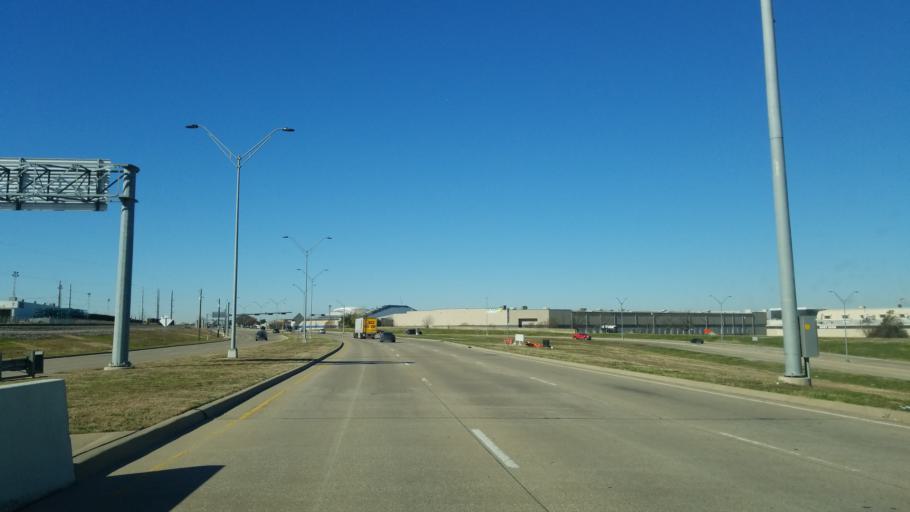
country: US
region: Texas
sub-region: Tarrant County
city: Arlington
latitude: 32.7431
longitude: -97.0632
